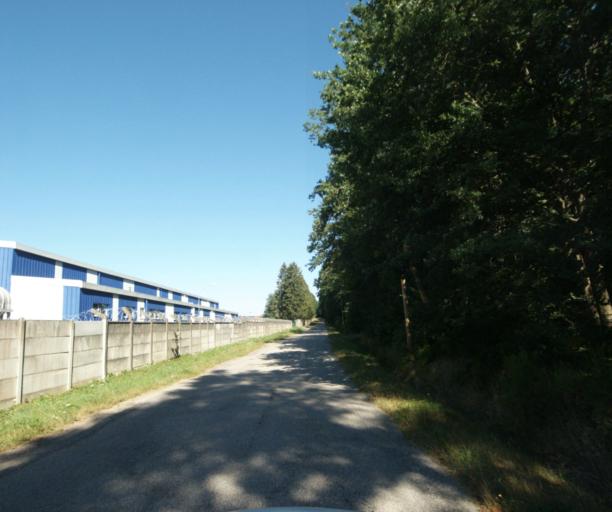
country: FR
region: Lorraine
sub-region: Departement des Vosges
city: Epinal
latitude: 48.1514
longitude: 6.4695
